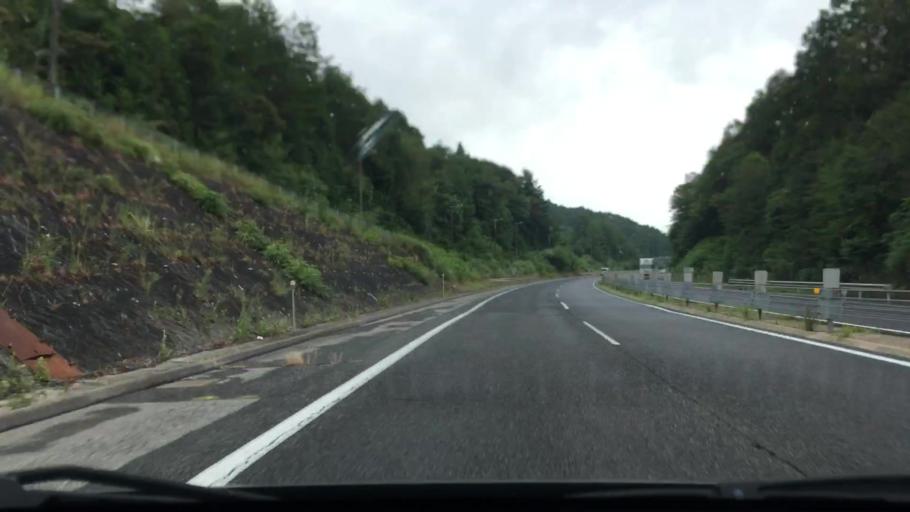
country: JP
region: Hiroshima
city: Hiroshima-shi
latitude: 34.6260
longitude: 132.5100
